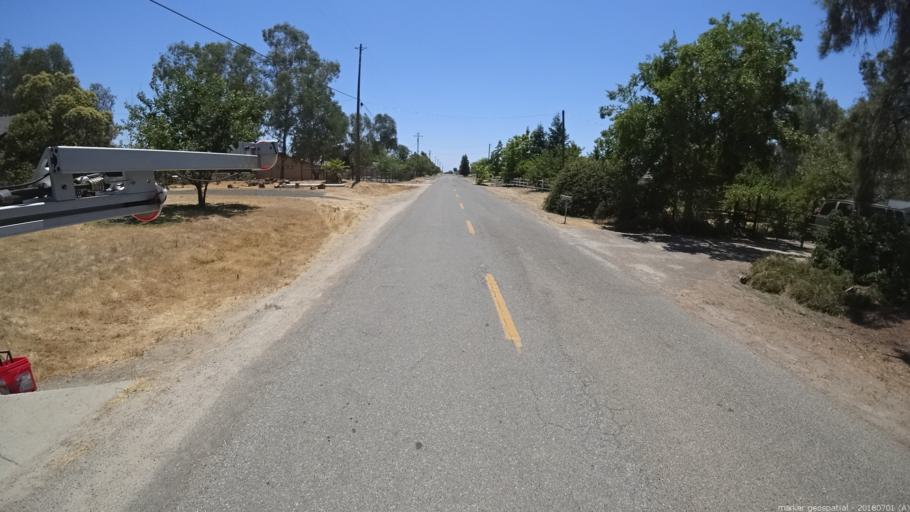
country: US
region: California
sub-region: Madera County
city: Madera Acres
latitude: 37.0446
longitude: -119.9867
